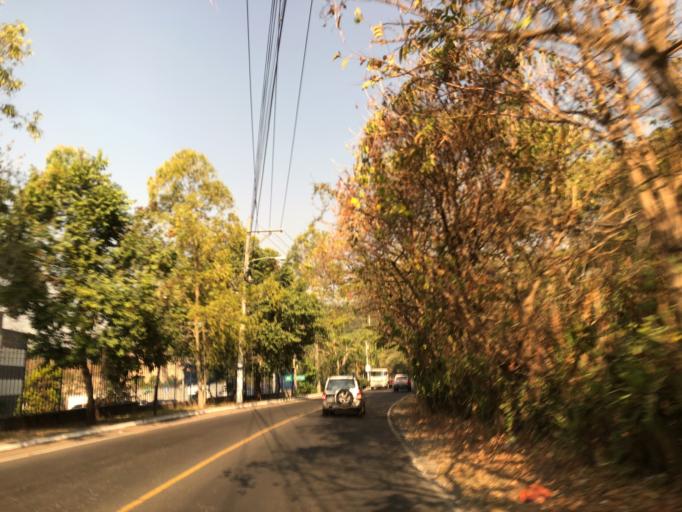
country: GT
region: Guatemala
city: Villa Canales
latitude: 14.4925
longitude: -90.5374
